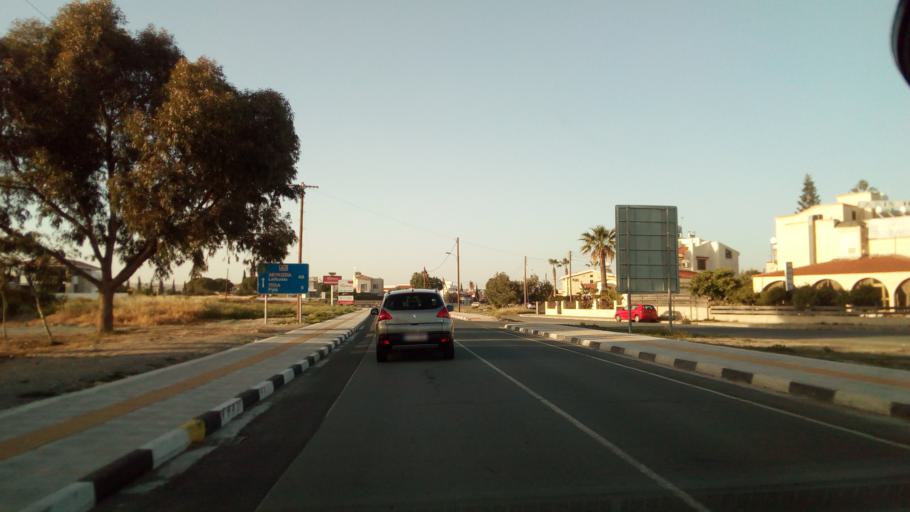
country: CY
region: Larnaka
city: Voroklini
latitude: 34.9737
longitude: 33.6730
